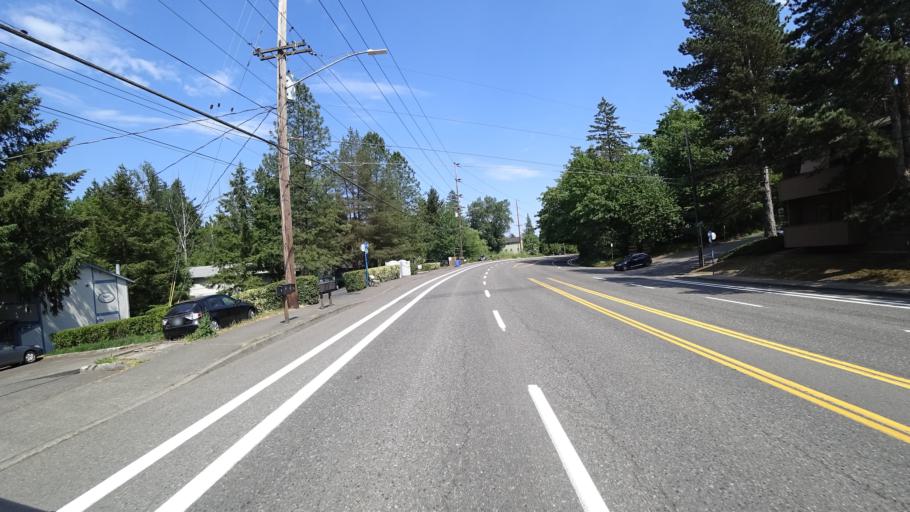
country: US
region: Oregon
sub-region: Washington County
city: Raleigh Hills
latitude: 45.4871
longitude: -122.7289
